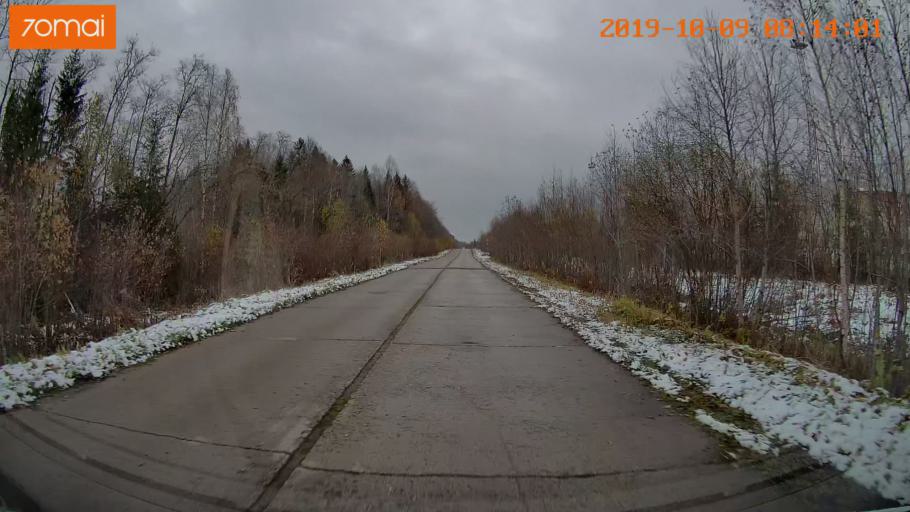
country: RU
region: Vologda
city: Gryazovets
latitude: 58.7264
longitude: 40.1488
